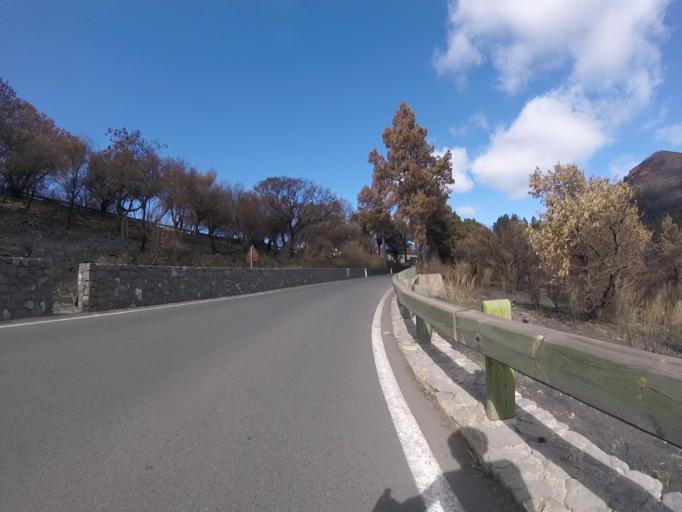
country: ES
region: Canary Islands
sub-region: Provincia de Las Palmas
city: Tejeda
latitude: 28.0053
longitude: -15.5984
